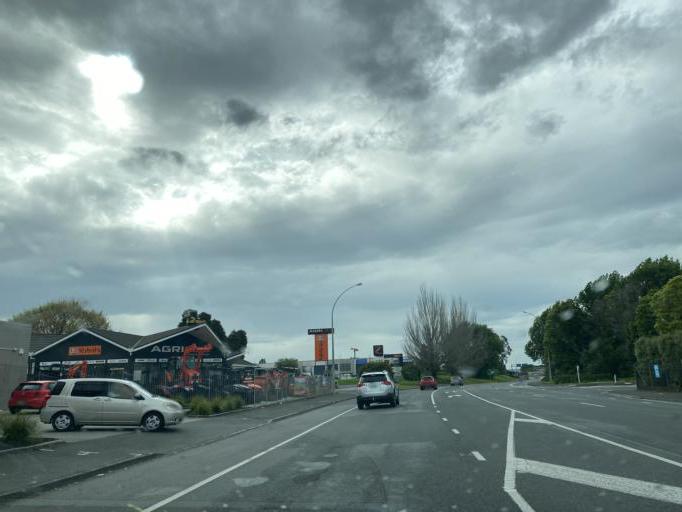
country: NZ
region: Waikato
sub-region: Hamilton City
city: Hamilton
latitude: -37.7861
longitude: 175.2561
